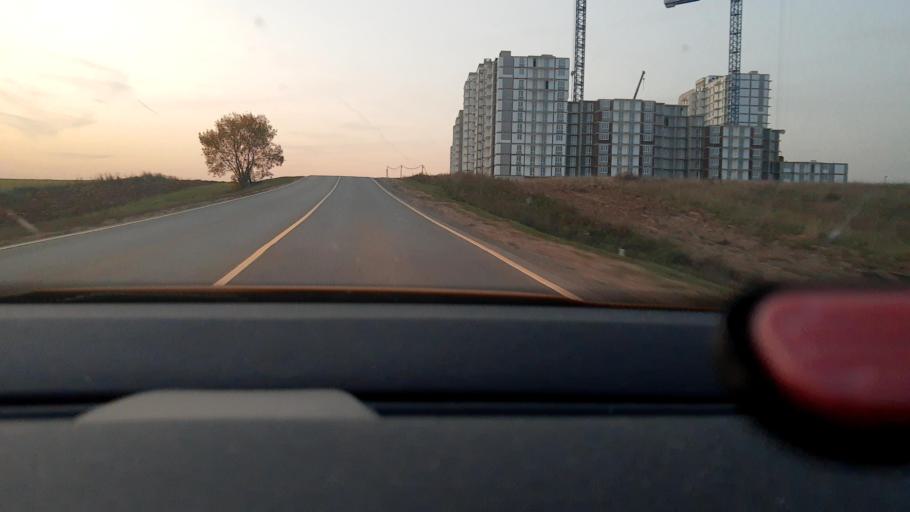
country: RU
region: Moskovskaya
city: Filimonki
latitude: 55.5298
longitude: 37.3795
